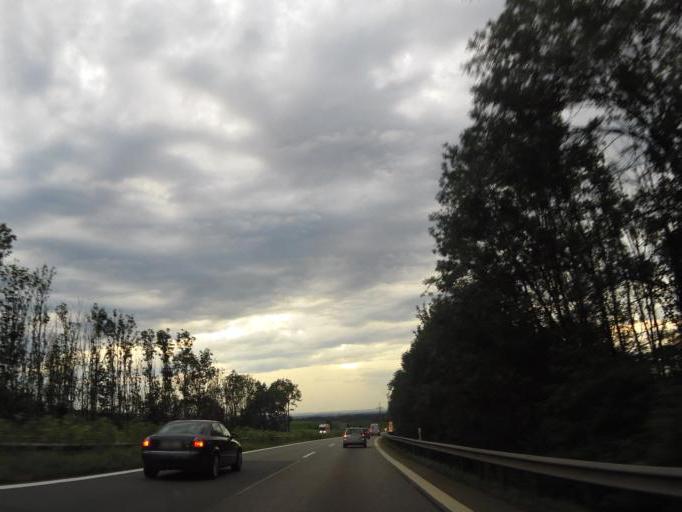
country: DE
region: Bavaria
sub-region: Upper Bavaria
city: Samerberg
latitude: 47.7970
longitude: 12.1975
